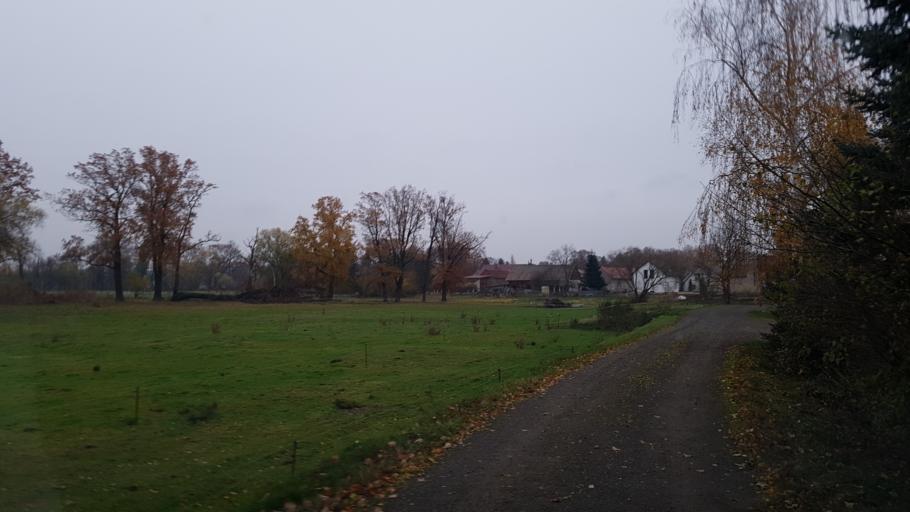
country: DE
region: Brandenburg
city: Falkenberg
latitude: 51.6332
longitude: 13.2826
